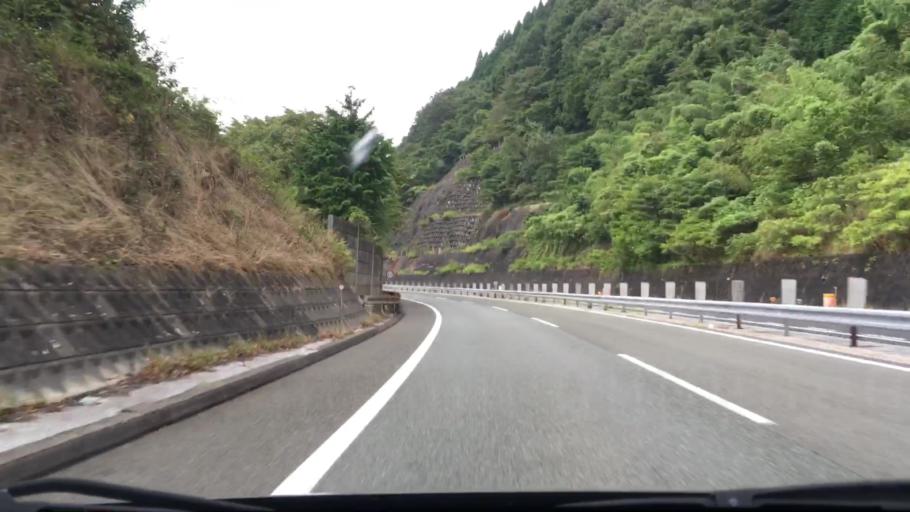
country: JP
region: Okayama
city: Niimi
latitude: 35.0149
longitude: 133.4321
